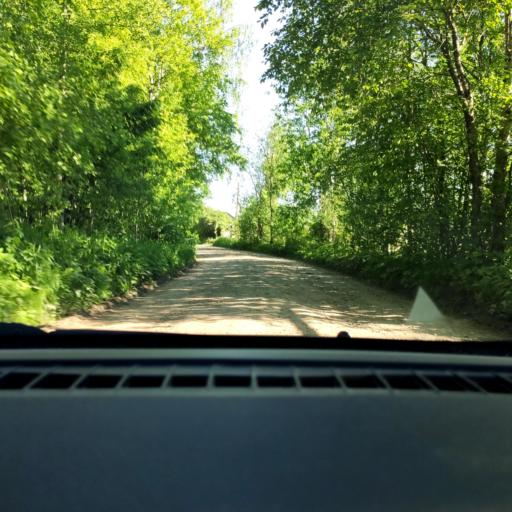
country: RU
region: Perm
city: Overyata
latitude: 58.1219
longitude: 55.8811
